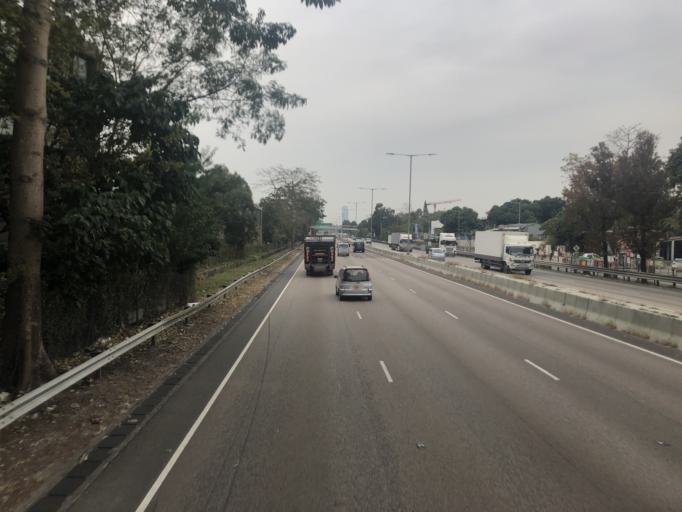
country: CN
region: Guangdong
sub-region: Shenzhen
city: Shenzhen
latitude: 22.5032
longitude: 114.1034
